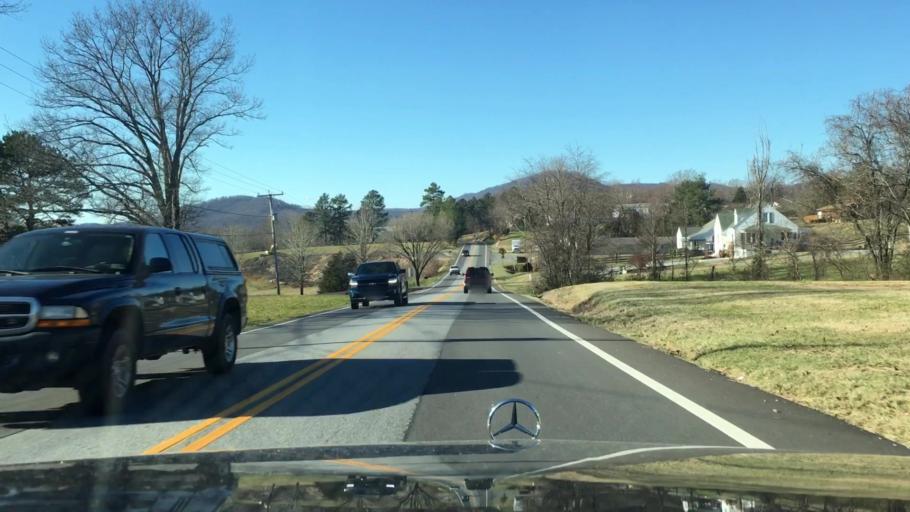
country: US
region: Virginia
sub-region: Botetourt County
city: Blue Ridge
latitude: 37.2694
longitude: -79.7630
